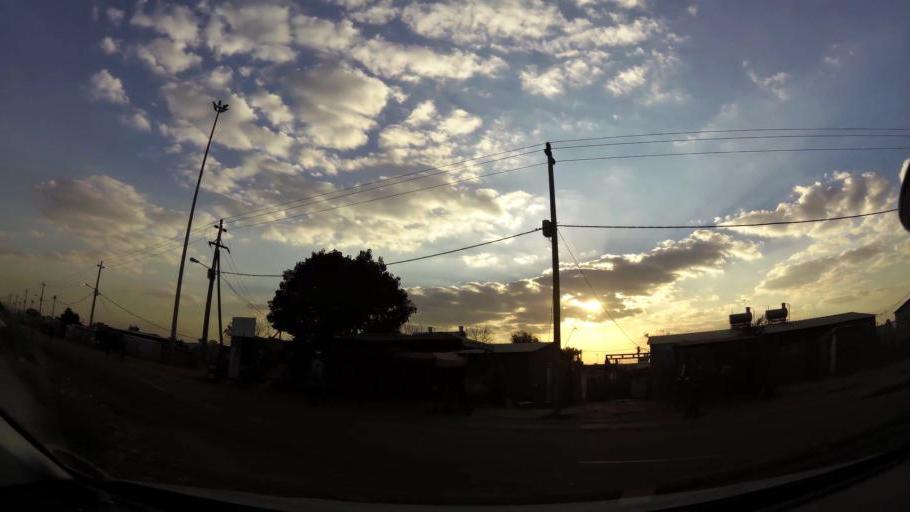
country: ZA
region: Gauteng
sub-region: City of Johannesburg Metropolitan Municipality
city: Soweto
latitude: -26.2637
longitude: 27.8978
